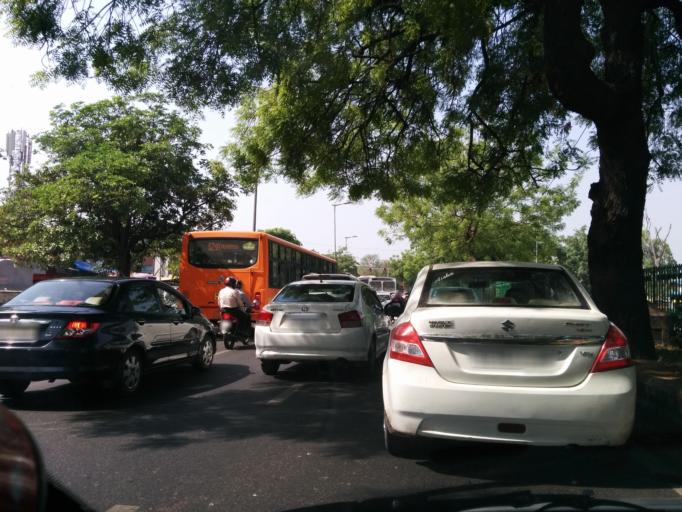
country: IN
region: NCT
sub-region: New Delhi
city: New Delhi
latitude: 28.5756
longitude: 77.2099
